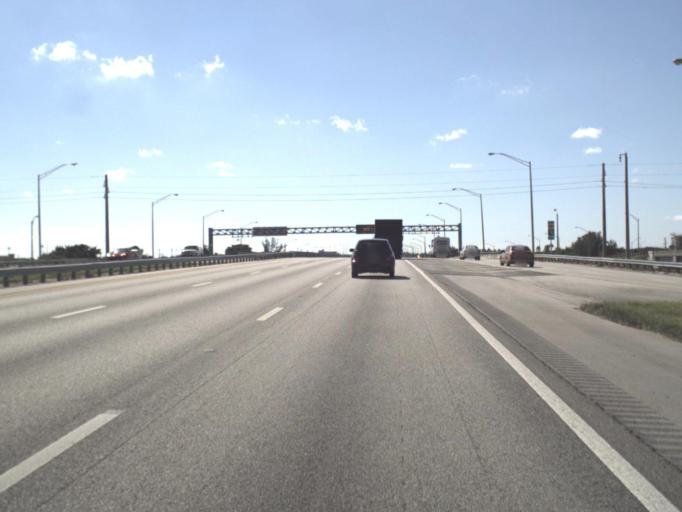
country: US
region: Florida
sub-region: Miami-Dade County
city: Sweetwater
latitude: 25.7696
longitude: -80.3858
